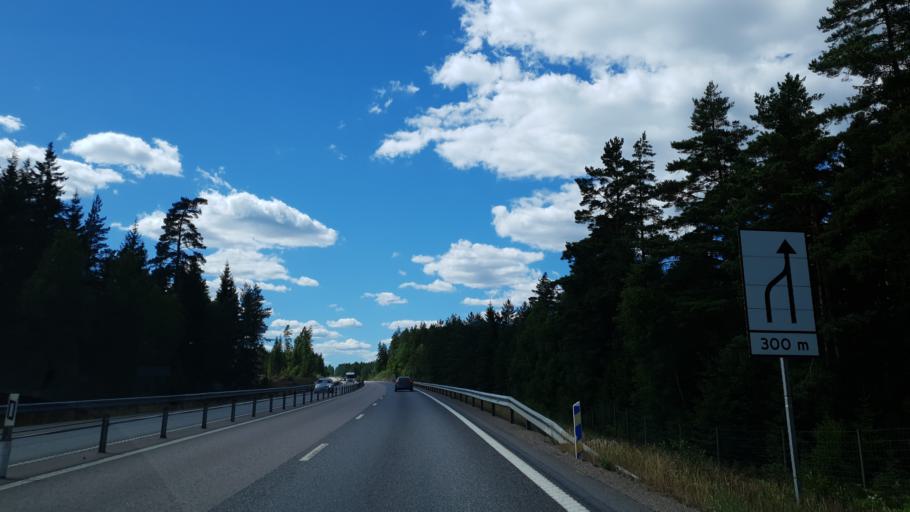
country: SE
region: Kronoberg
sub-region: Lessebo Kommun
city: Hovmantorp
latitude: 56.8689
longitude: 15.0072
